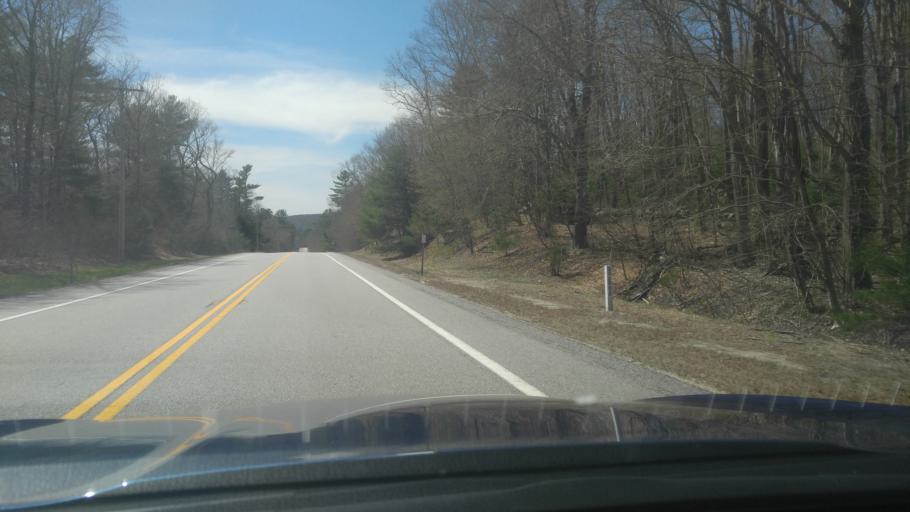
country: US
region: Rhode Island
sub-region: Kent County
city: West Greenwich
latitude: 41.5771
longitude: -71.6982
